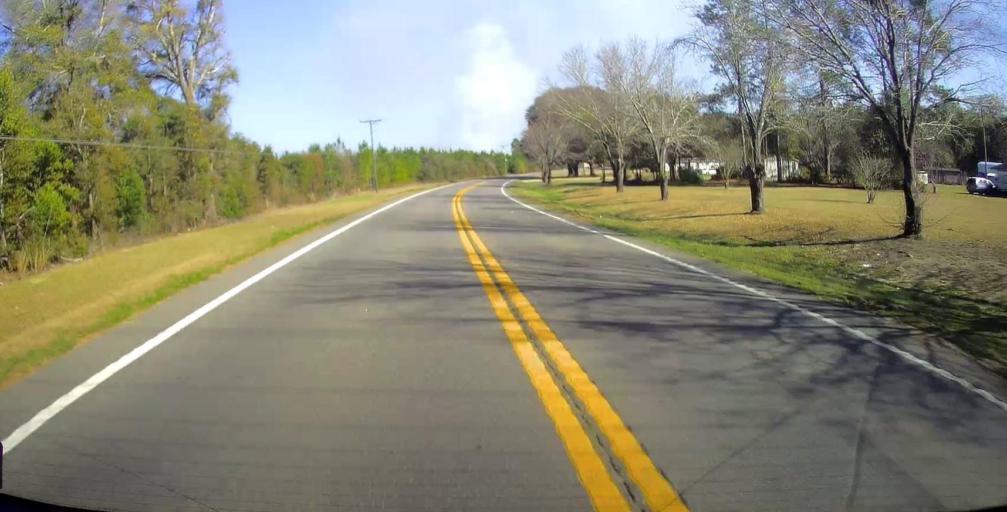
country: US
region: Georgia
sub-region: Macon County
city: Oglethorpe
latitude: 32.3292
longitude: -84.0754
